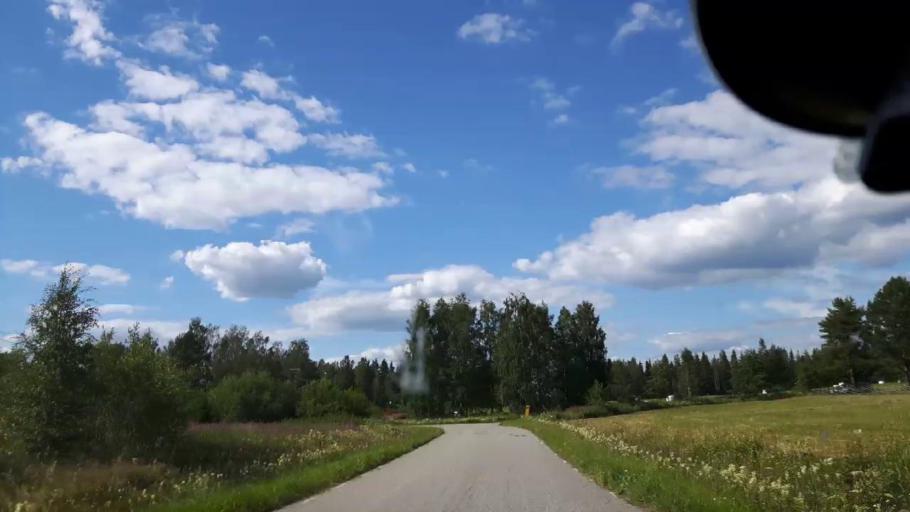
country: SE
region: Jaemtland
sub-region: Braecke Kommun
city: Braecke
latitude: 62.8289
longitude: 15.3065
